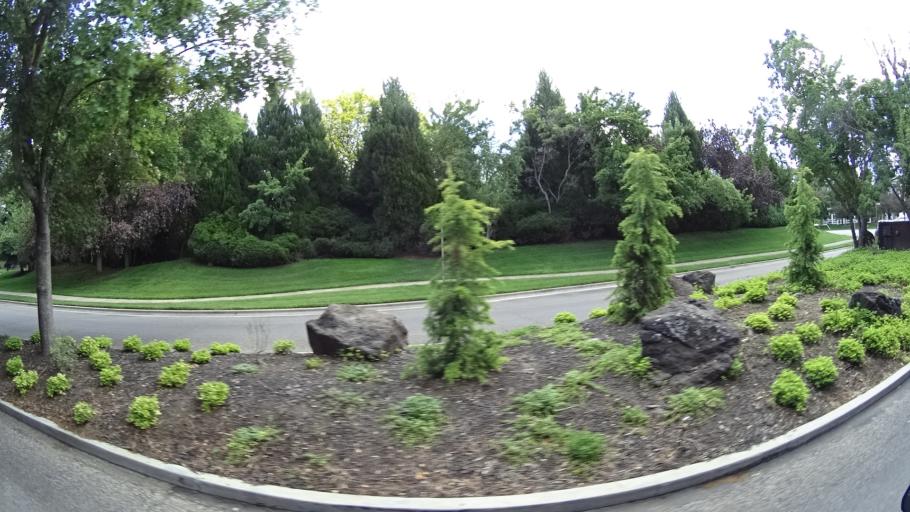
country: US
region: Idaho
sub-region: Ada County
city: Boise
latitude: 43.5898
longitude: -116.1735
